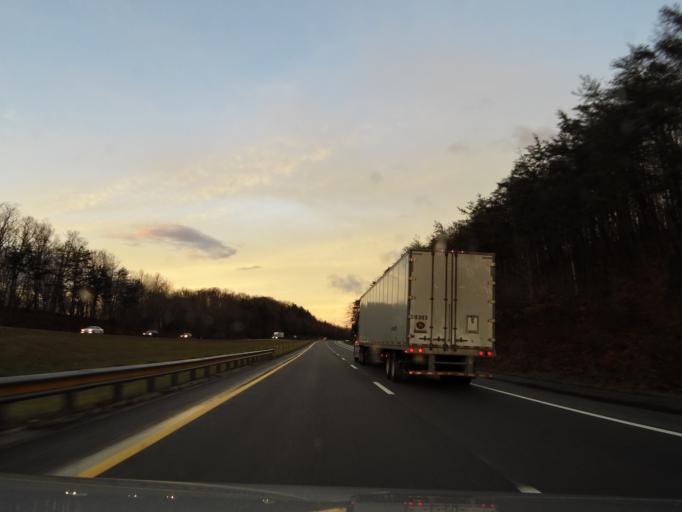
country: US
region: Tennessee
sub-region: Campbell County
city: Jacksboro
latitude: 36.4620
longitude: -84.2511
